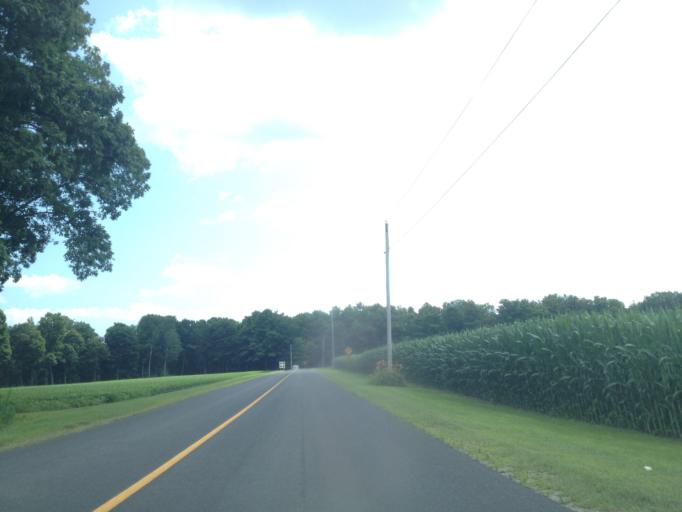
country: CA
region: Ontario
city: Aylmer
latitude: 42.6792
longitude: -81.0180
